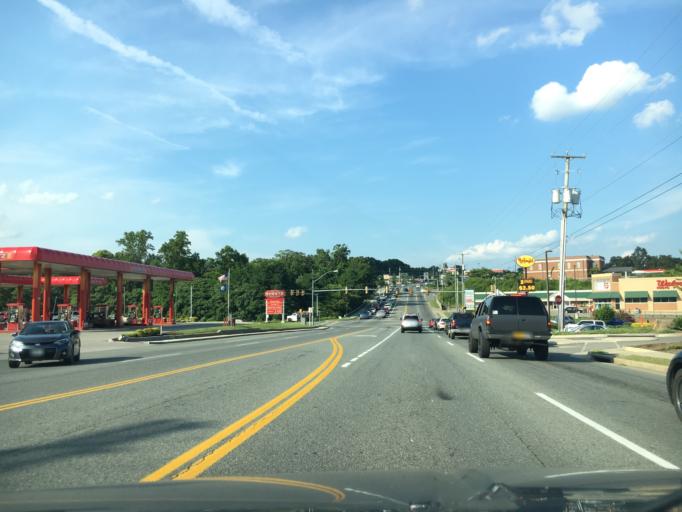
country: US
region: Virginia
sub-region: Franklin County
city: Rocky Mount
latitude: 37.0116
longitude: -79.8697
